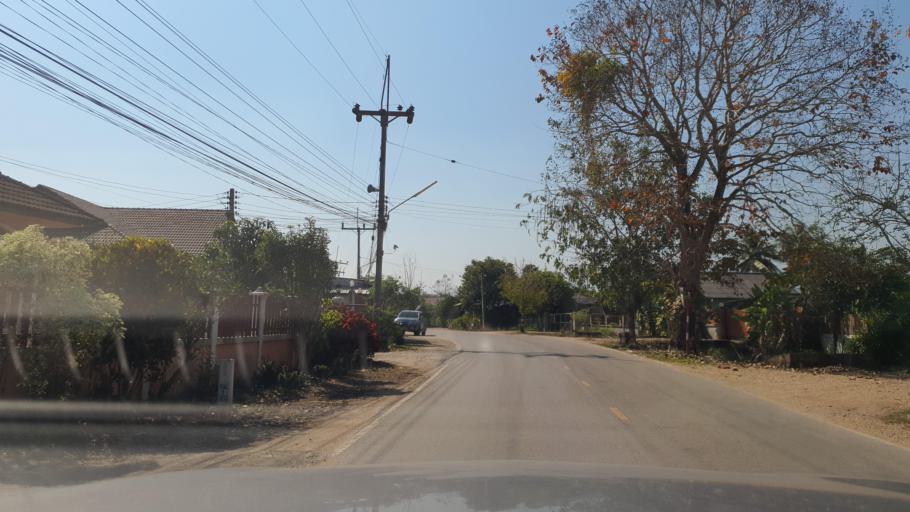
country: TH
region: Chiang Rai
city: Mae Lao
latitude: 19.7635
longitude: 99.7216
